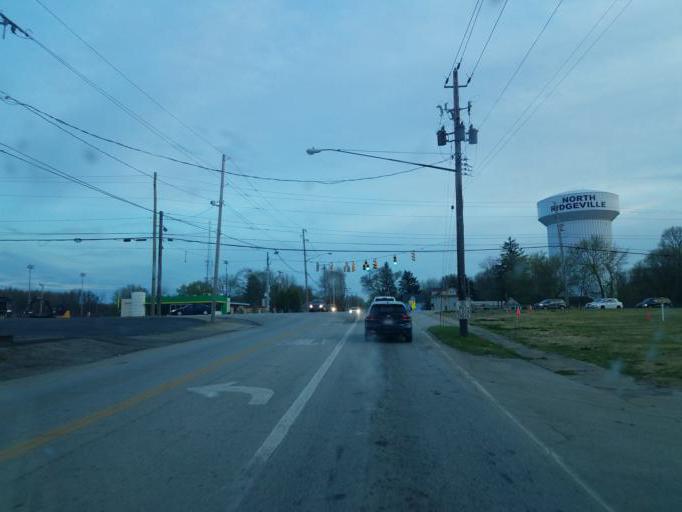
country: US
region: Ohio
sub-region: Lorain County
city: North Ridgeville
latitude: 41.3908
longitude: -82.0187
